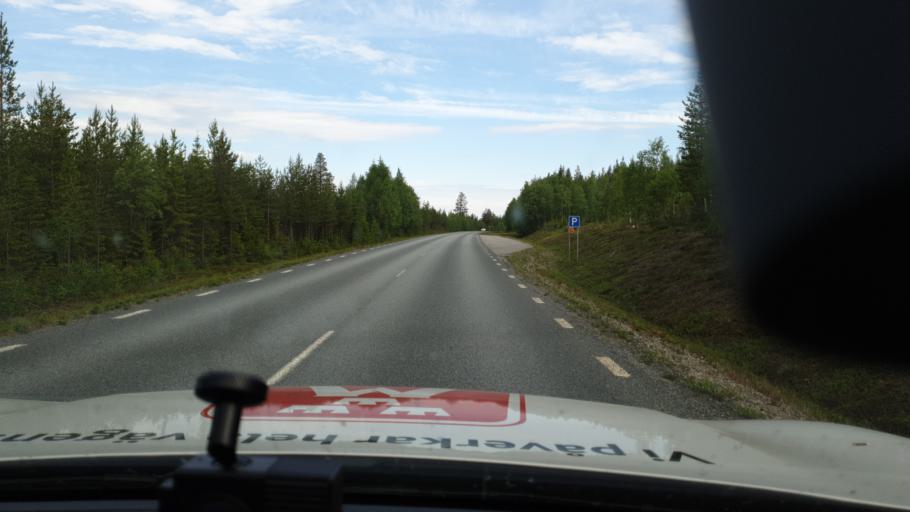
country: SE
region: Vaesterbotten
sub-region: Lycksele Kommun
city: Soderfors
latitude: 65.1392
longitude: 18.2670
